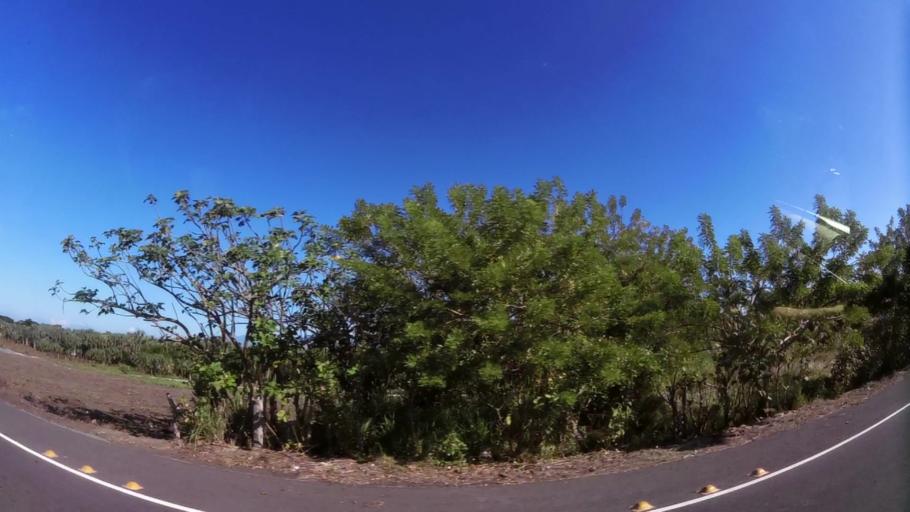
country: GT
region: Santa Rosa
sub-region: Municipio de Taxisco
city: Taxisco
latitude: 13.8743
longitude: -90.4273
